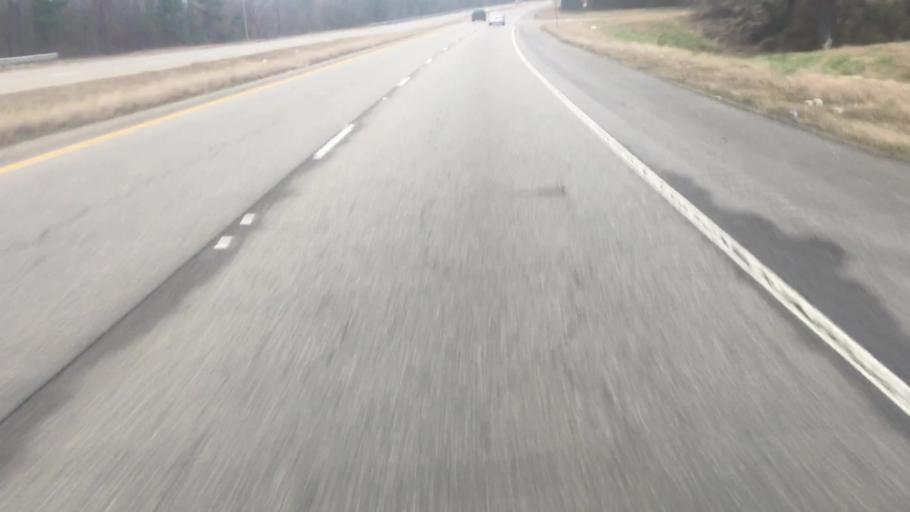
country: US
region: Alabama
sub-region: Walker County
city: Cordova
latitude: 33.8181
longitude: -87.1513
